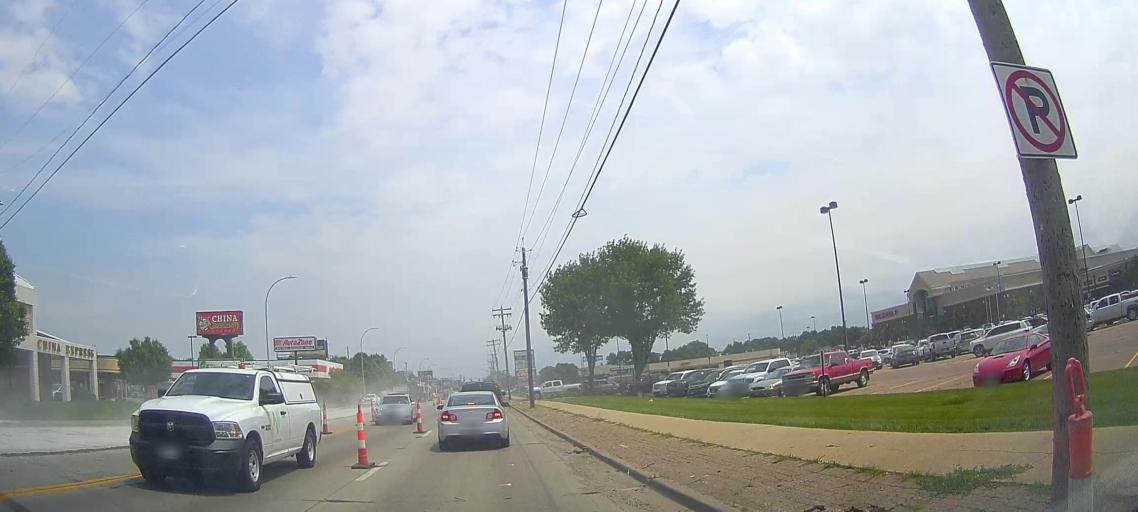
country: US
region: South Dakota
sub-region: Minnehaha County
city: Sioux Falls
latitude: 43.5148
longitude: -96.7544
